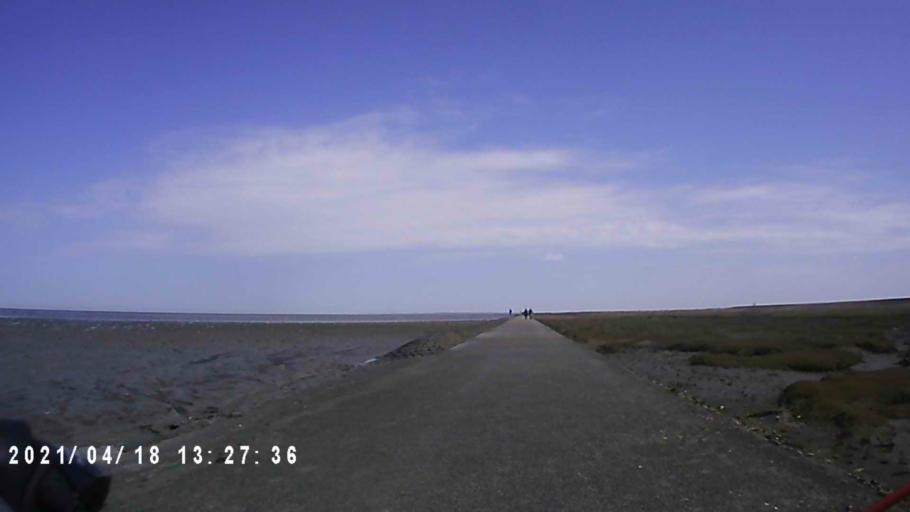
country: NL
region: Friesland
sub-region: Gemeente Dongeradeel
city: Anjum
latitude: 53.4056
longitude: 6.0874
